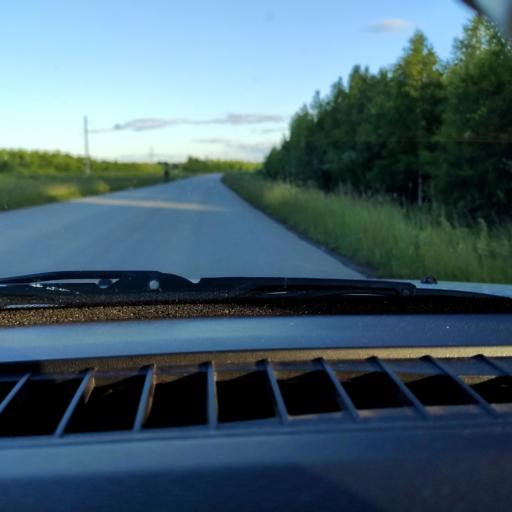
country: RU
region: Perm
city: Polazna
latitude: 58.2067
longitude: 56.5300
